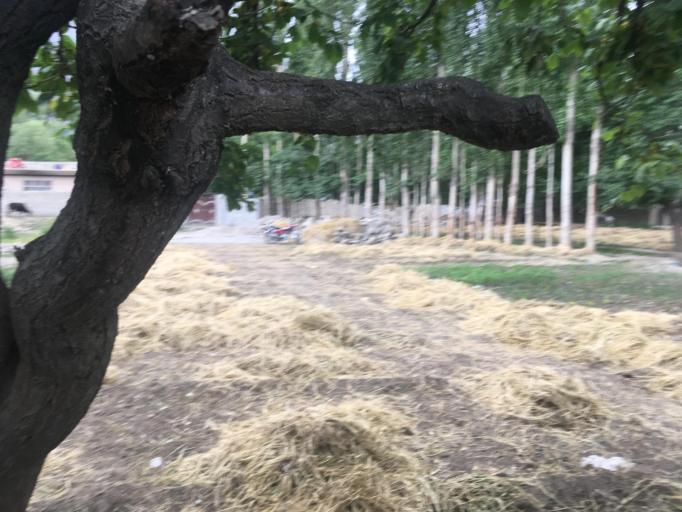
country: PK
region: Gilgit-Baltistan
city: Skardu
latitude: 35.2927
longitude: 75.6492
